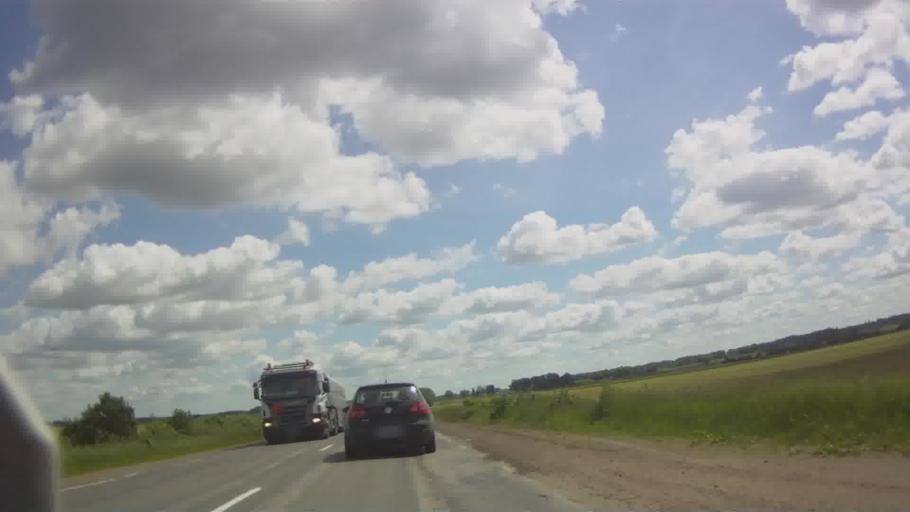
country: LV
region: Vilanu
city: Vilani
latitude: 56.6021
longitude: 26.8609
